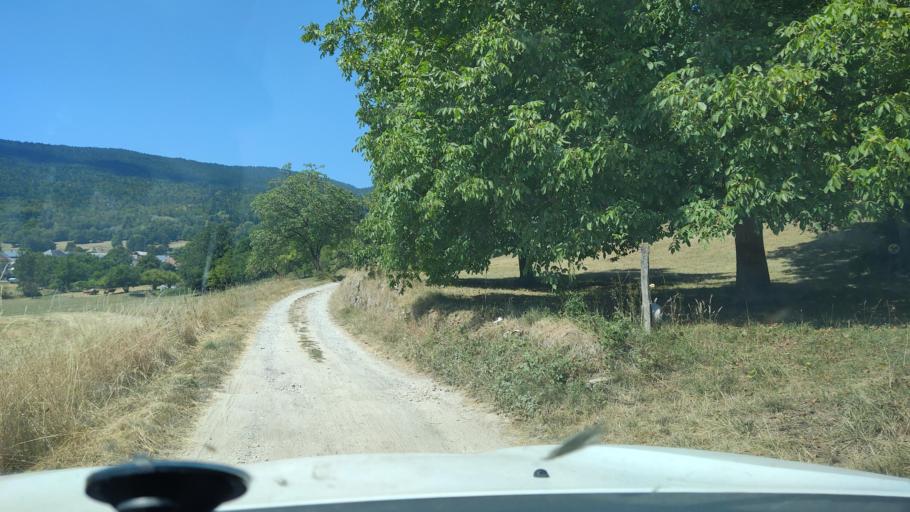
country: FR
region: Rhone-Alpes
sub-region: Departement de la Haute-Savoie
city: Cusy
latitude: 45.7215
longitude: 6.0793
